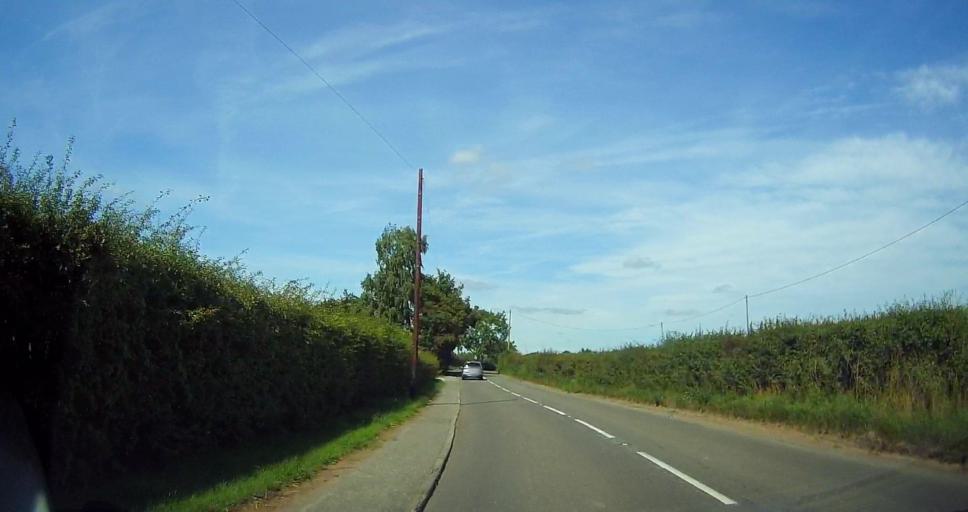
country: GB
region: England
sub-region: Shropshire
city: Market Drayton
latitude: 52.9782
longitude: -2.5130
